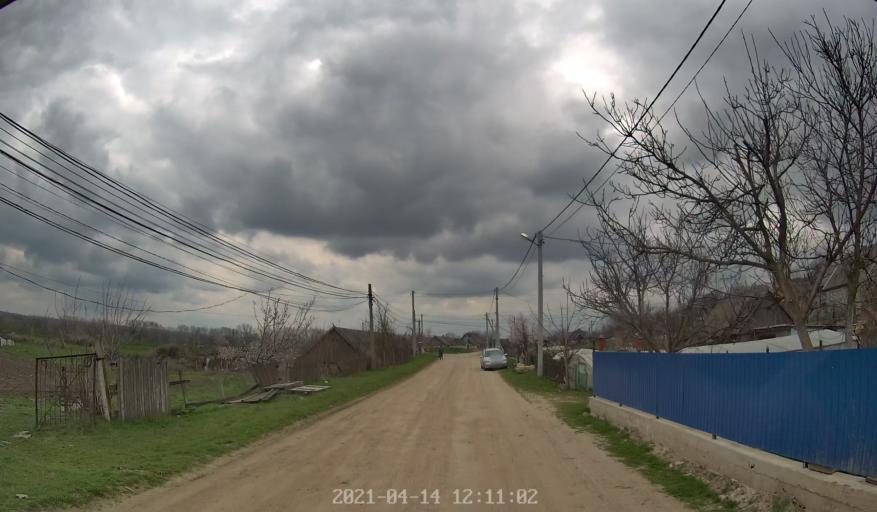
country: MD
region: Criuleni
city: Criuleni
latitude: 47.1673
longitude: 29.2046
